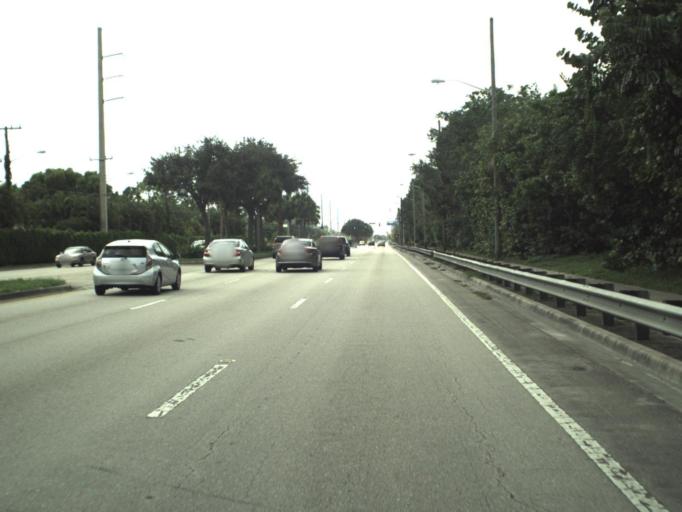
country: US
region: Florida
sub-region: Palm Beach County
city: Greenacres City
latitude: 26.6410
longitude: -80.1458
